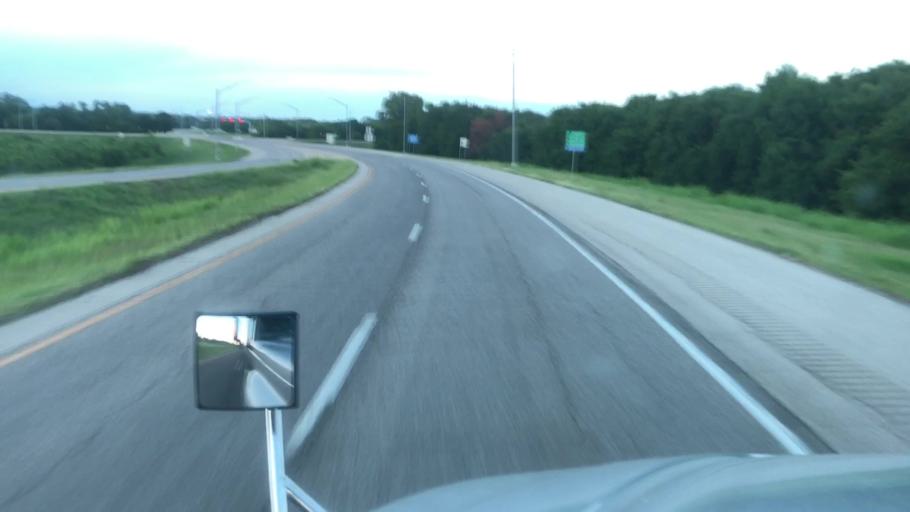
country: US
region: Oklahoma
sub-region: Kay County
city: Ponca City
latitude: 36.6777
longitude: -97.0707
